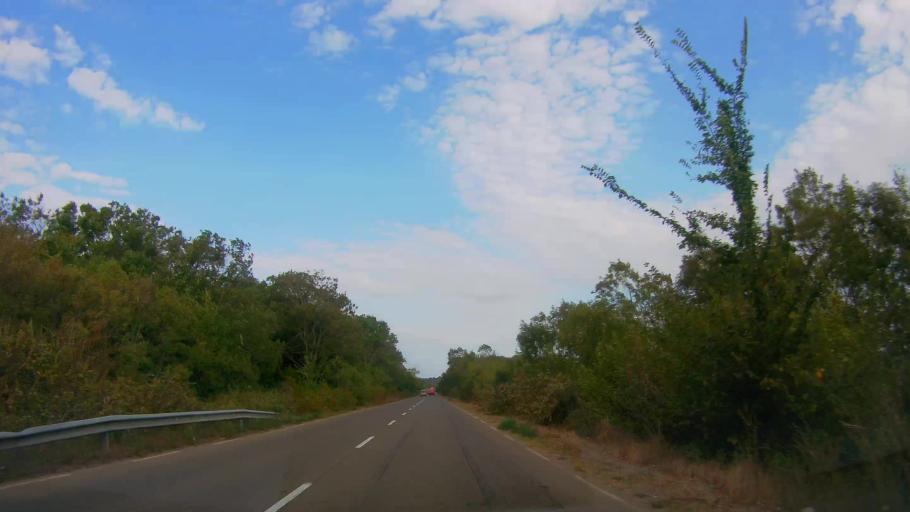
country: BG
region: Burgas
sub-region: Obshtina Sozopol
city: Sozopol
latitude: 42.3512
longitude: 27.7102
